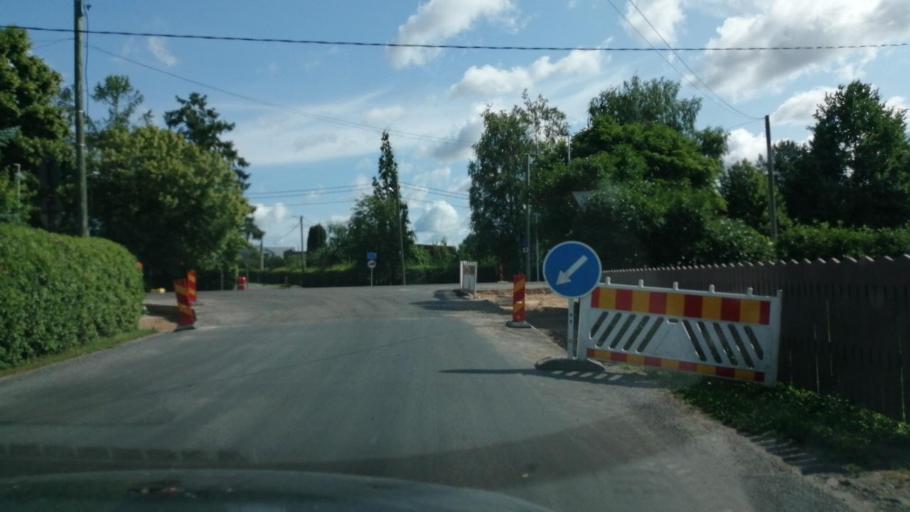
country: EE
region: Viljandimaa
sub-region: Viiratsi vald
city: Viiratsi
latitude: 58.3604
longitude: 25.6441
